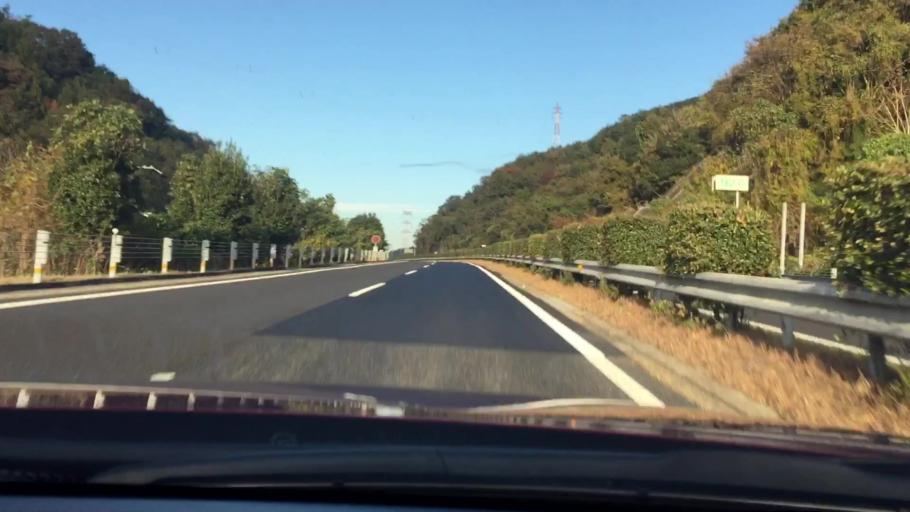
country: JP
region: Hyogo
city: Yamazakicho-nakabirose
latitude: 34.9796
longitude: 134.6240
